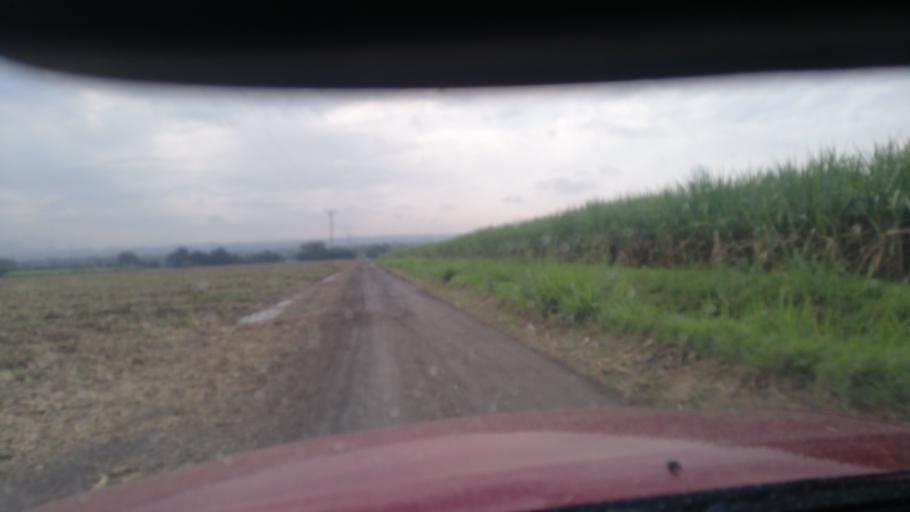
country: CO
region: Risaralda
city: La Virginia
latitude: 4.8751
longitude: -75.9242
